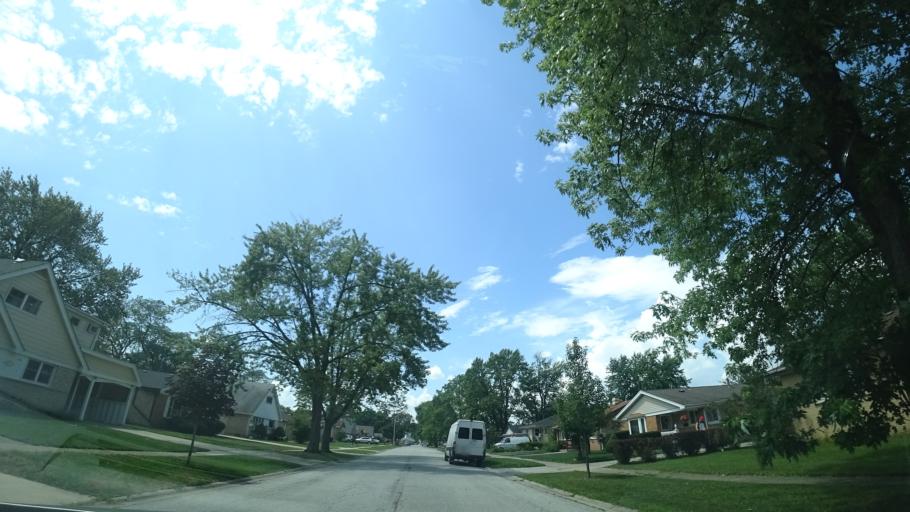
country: US
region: Illinois
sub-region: Cook County
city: Alsip
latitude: 41.6660
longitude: -87.7298
